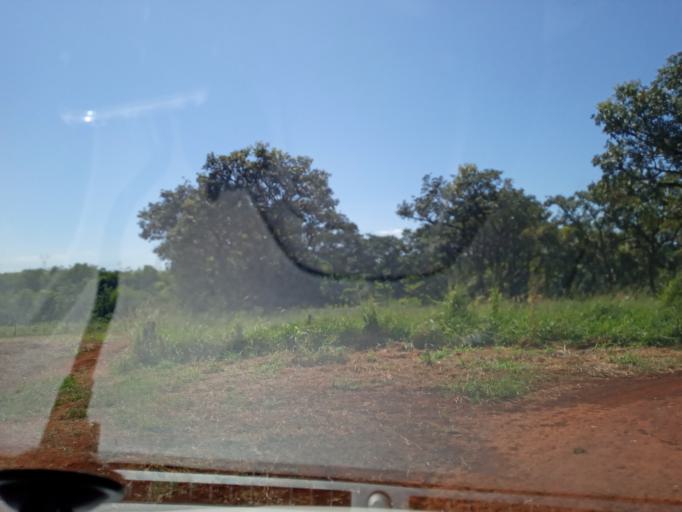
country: BR
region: Goias
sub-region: Itumbiara
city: Itumbiara
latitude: -18.4446
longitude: -49.1434
